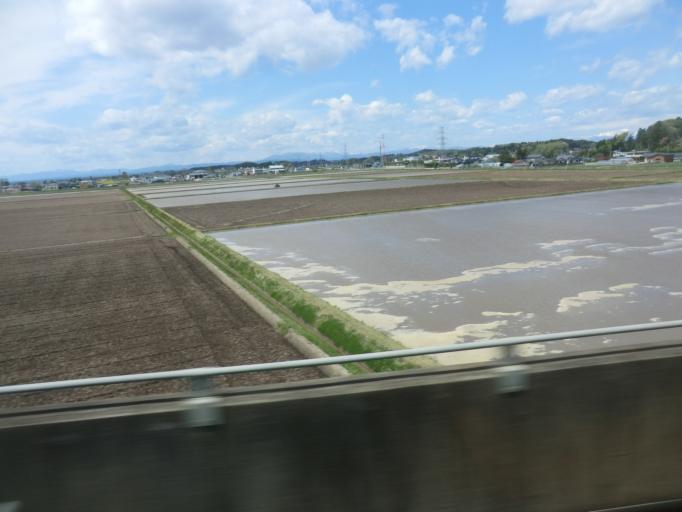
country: JP
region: Miyagi
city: Furukawa
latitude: 38.6117
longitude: 140.9904
